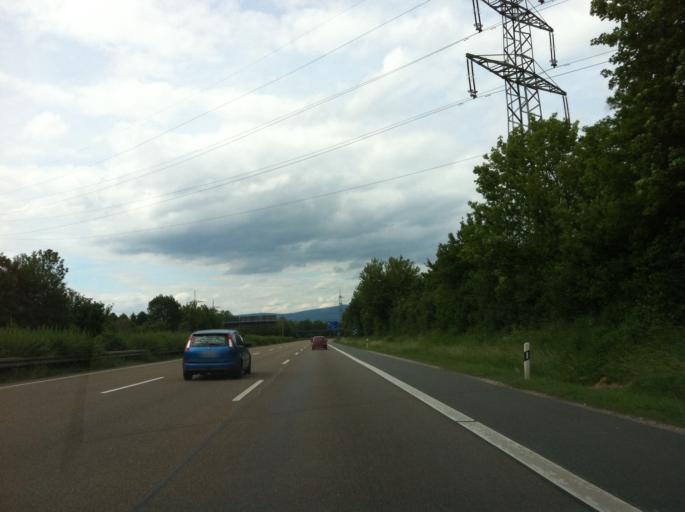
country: DE
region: Hesse
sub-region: Regierungsbezirk Darmstadt
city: Hattersheim
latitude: 50.0904
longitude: 8.4845
